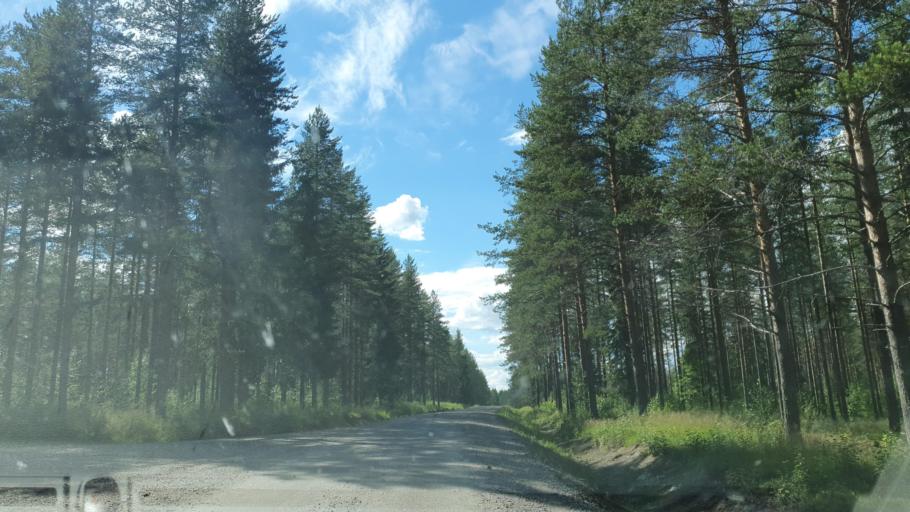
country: FI
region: Kainuu
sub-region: Kehys-Kainuu
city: Kuhmo
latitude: 64.1457
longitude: 29.7764
